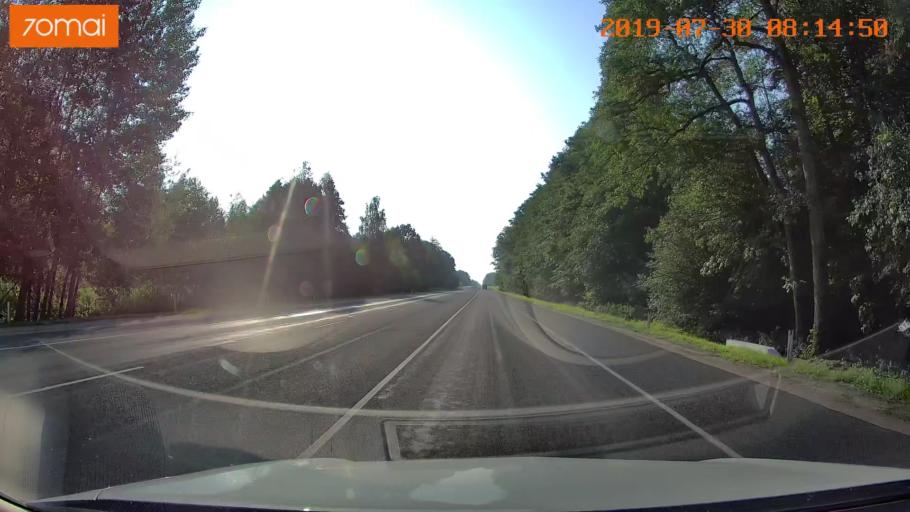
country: RU
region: Kaliningrad
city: Zheleznodorozhnyy
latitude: 54.6466
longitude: 21.3685
